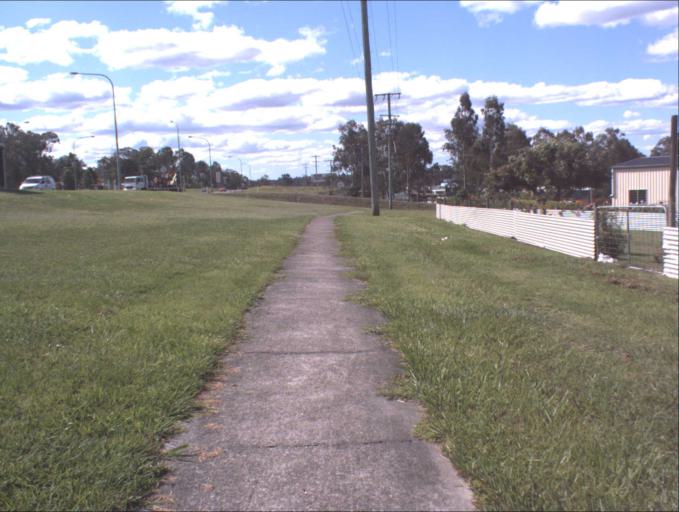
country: AU
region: Queensland
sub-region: Logan
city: Cedar Vale
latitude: -27.8309
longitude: 153.0291
